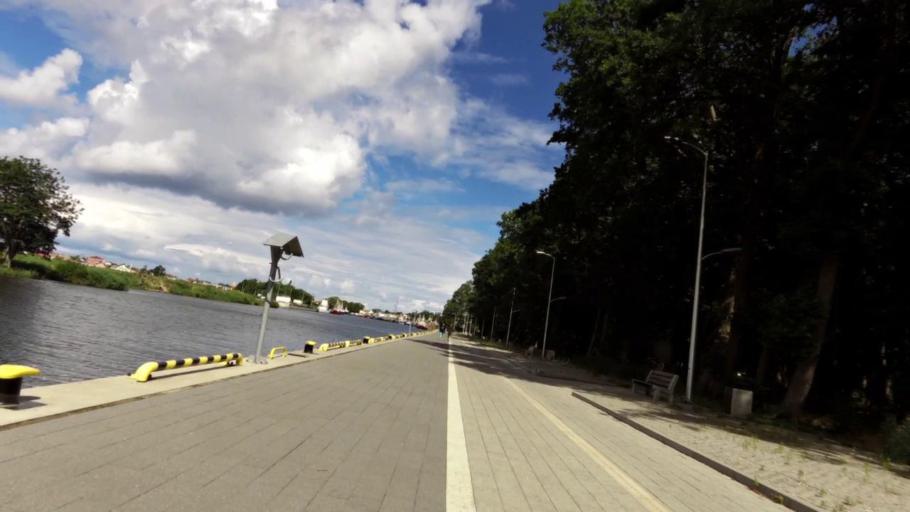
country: PL
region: West Pomeranian Voivodeship
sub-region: Powiat slawienski
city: Darlowo
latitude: 54.4329
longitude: 16.3908
